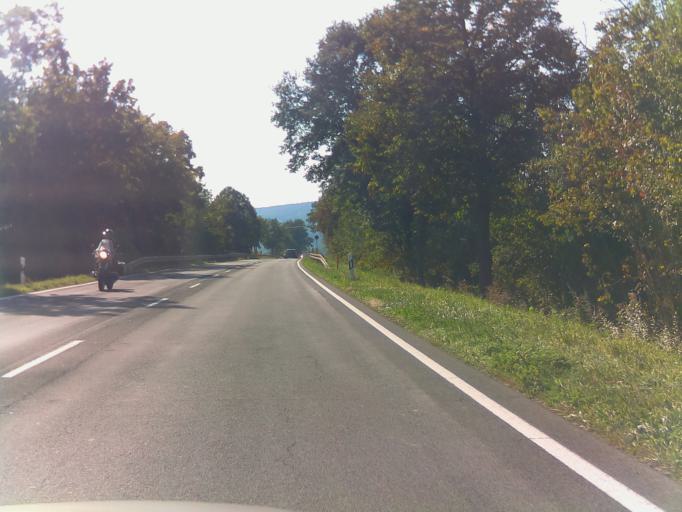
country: DE
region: Bavaria
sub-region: Regierungsbezirk Unterfranken
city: Untermerzbach
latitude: 50.1227
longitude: 10.8796
